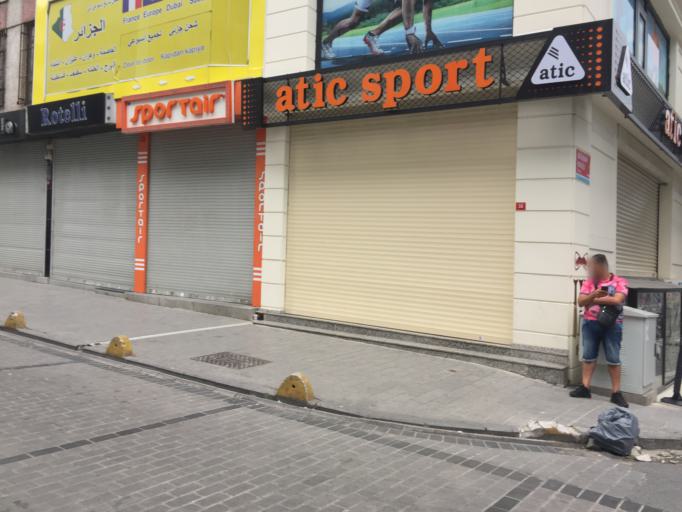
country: TR
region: Istanbul
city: Istanbul
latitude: 41.0084
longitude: 28.9617
